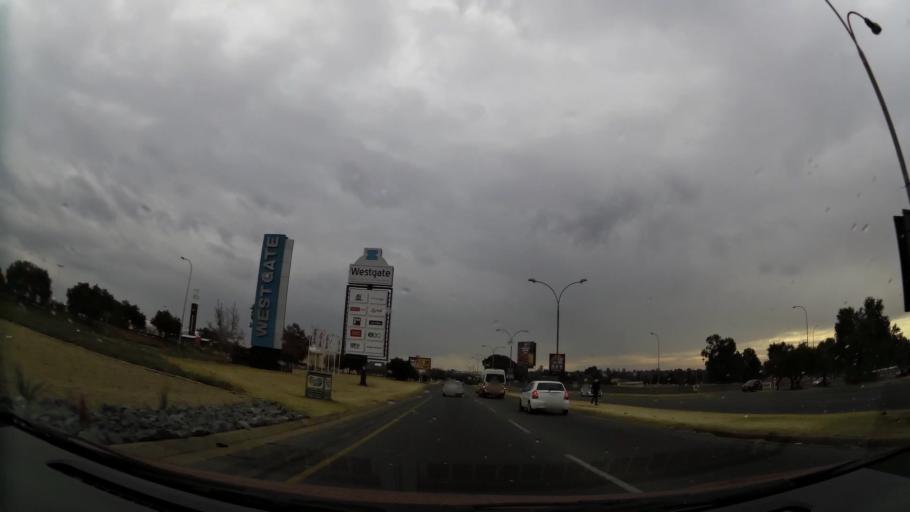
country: ZA
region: Gauteng
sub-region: City of Johannesburg Metropolitan Municipality
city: Roodepoort
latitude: -26.1382
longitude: 27.8640
